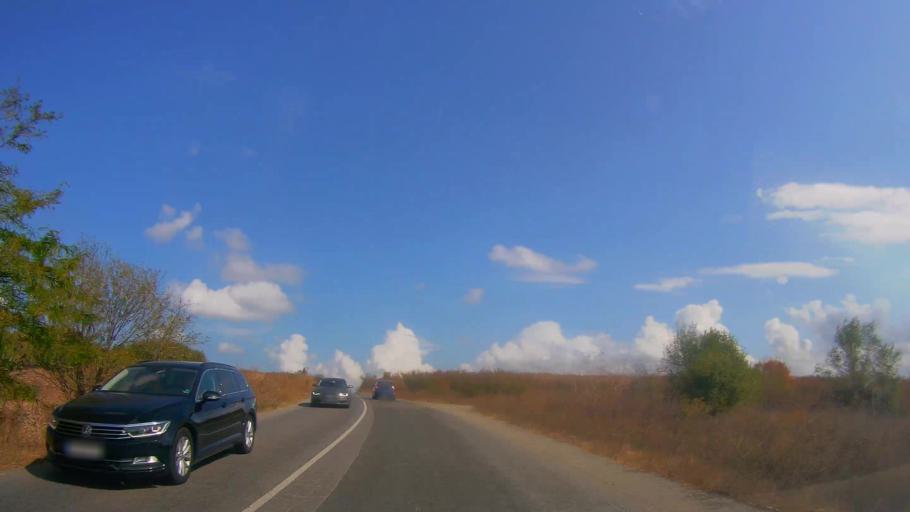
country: BG
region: Burgas
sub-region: Obshtina Burgas
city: Burgas
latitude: 42.4772
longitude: 27.3910
